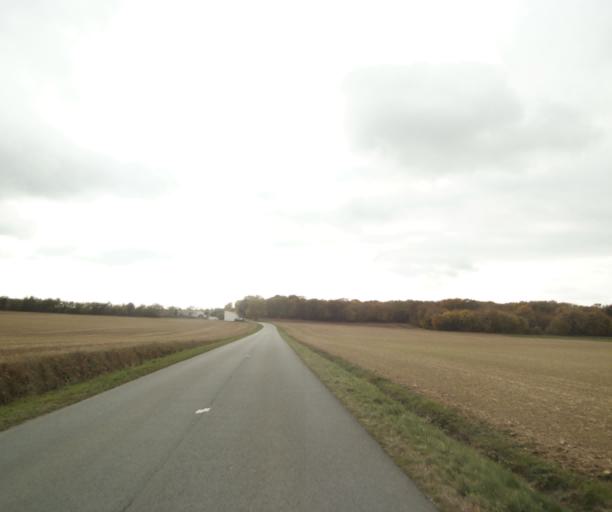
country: FR
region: Poitou-Charentes
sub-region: Departement de la Charente-Maritime
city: Saint-Georges-des-Coteaux
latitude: 45.7747
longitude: -0.7044
